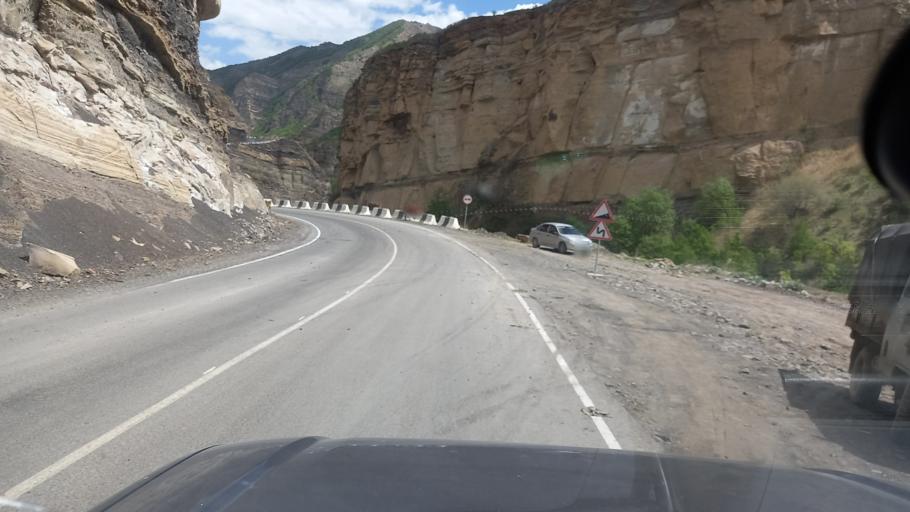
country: RU
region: Dagestan
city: Gunib
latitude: 42.3201
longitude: 46.9314
